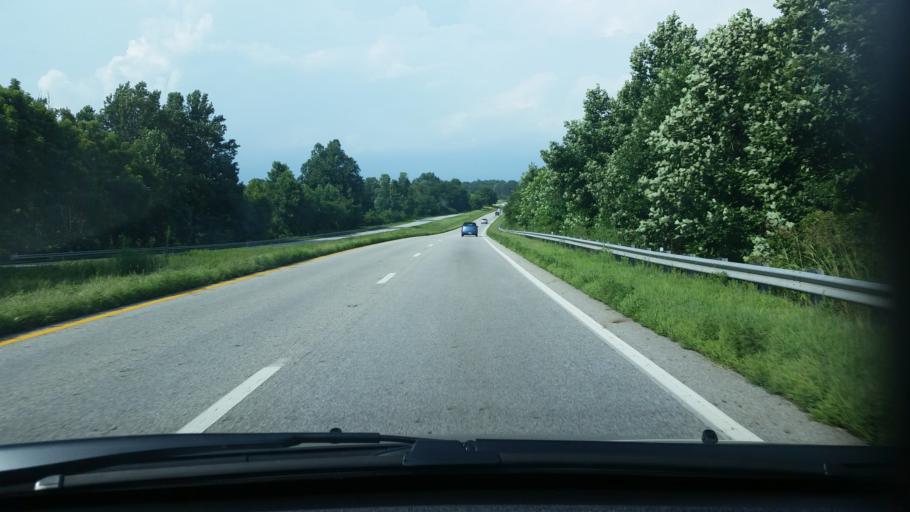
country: US
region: Virginia
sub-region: Nelson County
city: Lovingston
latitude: 37.7246
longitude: -78.8992
